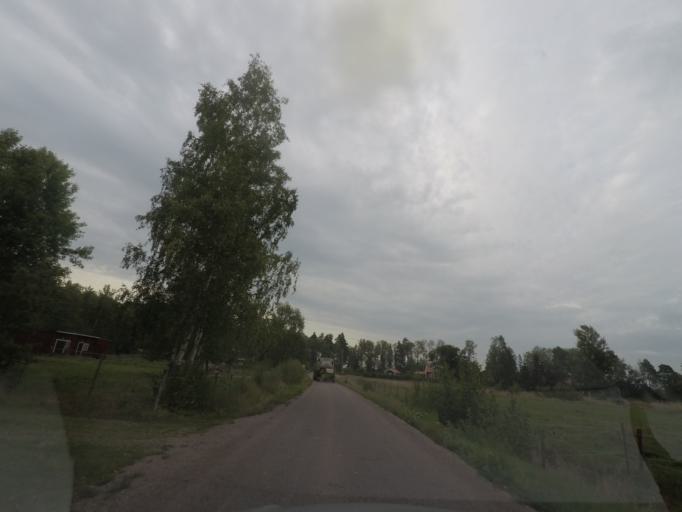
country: SE
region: Vaestmanland
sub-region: Hallstahammars Kommun
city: Kolback
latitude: 59.5017
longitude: 16.1907
